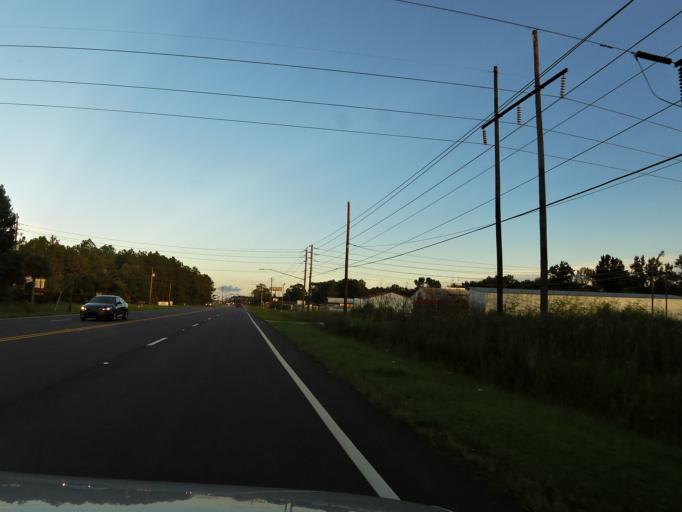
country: US
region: Georgia
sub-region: Camden County
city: Kingsland
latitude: 30.7964
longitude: -81.6726
